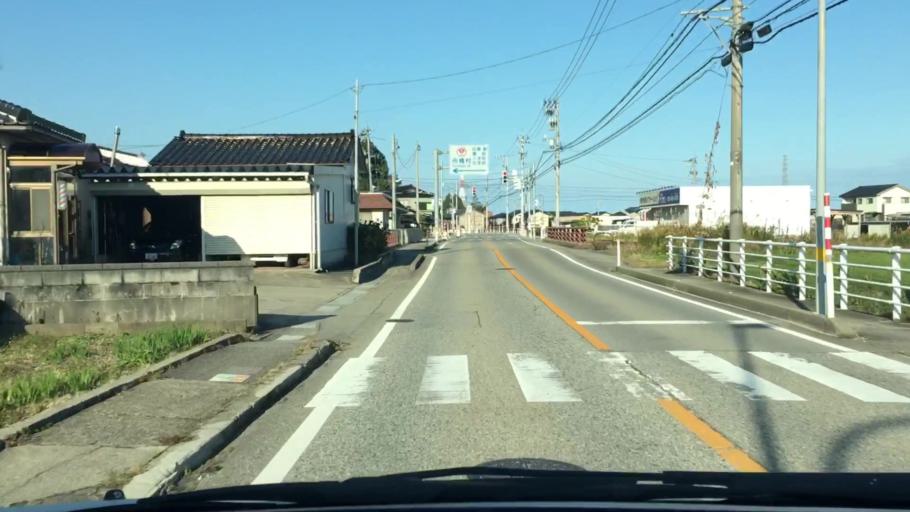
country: JP
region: Toyama
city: Kamiichi
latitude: 36.7056
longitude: 137.3101
